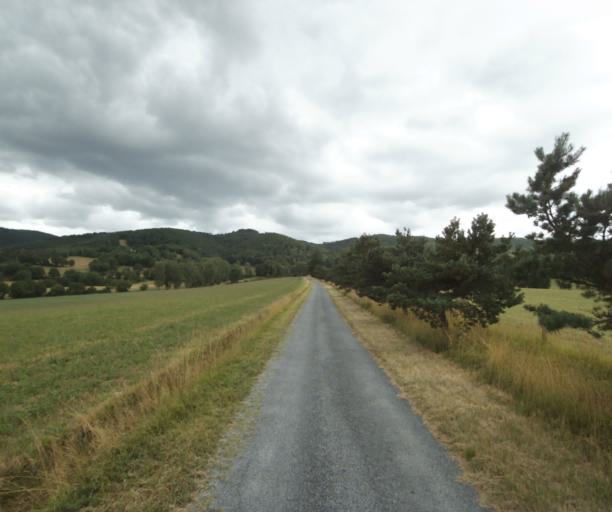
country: FR
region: Midi-Pyrenees
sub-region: Departement du Tarn
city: Soreze
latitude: 43.4635
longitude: 2.0865
